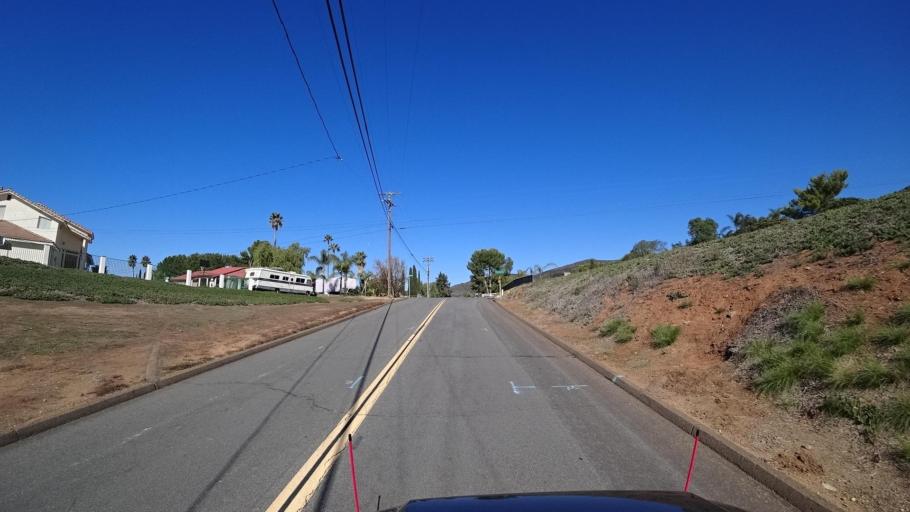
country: US
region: California
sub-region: San Diego County
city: Jamul
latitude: 32.7347
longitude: -116.8540
